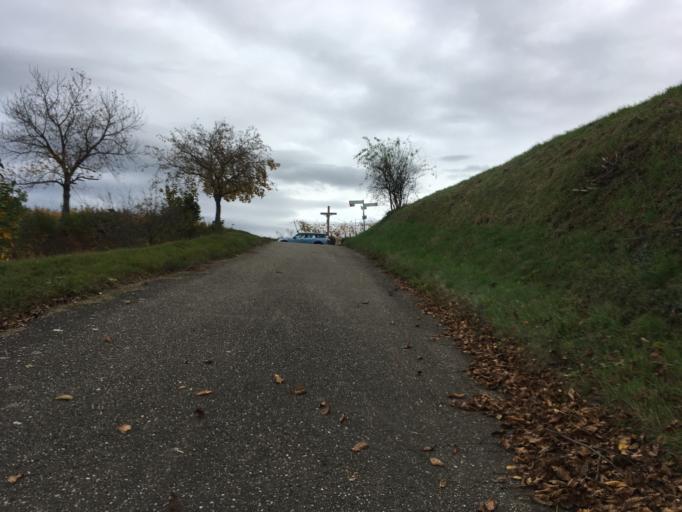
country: DE
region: Baden-Wuerttemberg
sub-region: Freiburg Region
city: Merdingen
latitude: 48.0163
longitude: 7.6982
